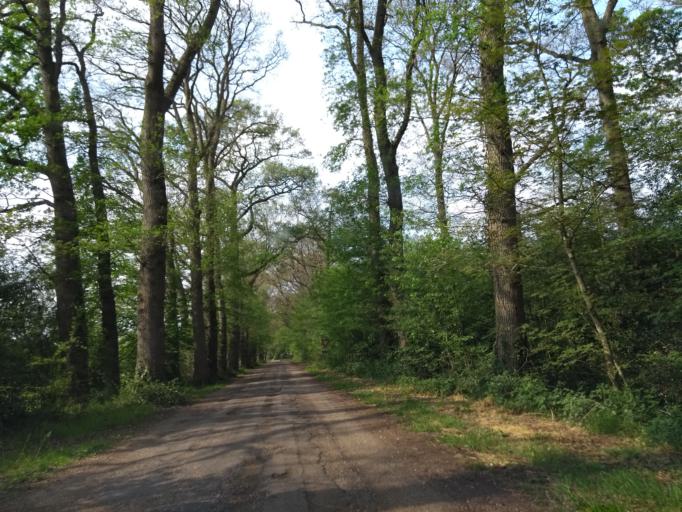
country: NL
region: Overijssel
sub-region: Gemeente Staphorst
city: Staphorst
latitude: 52.6717
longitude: 6.2733
